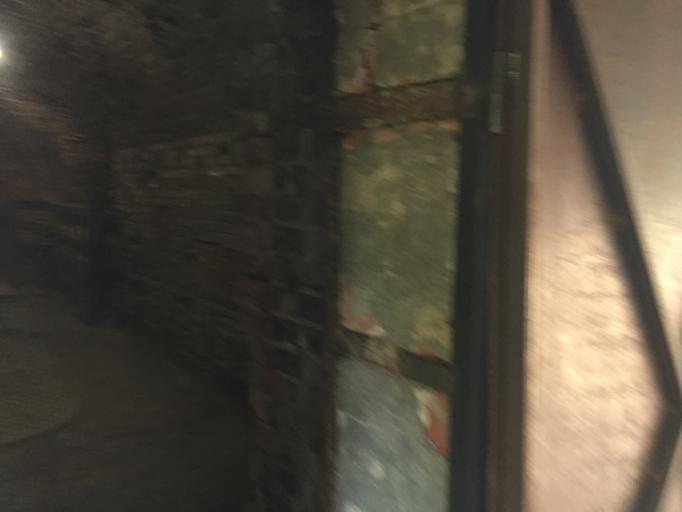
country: RU
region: Kaliningrad
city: Bol'shoe Isakovo
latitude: 54.6566
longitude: 20.5678
